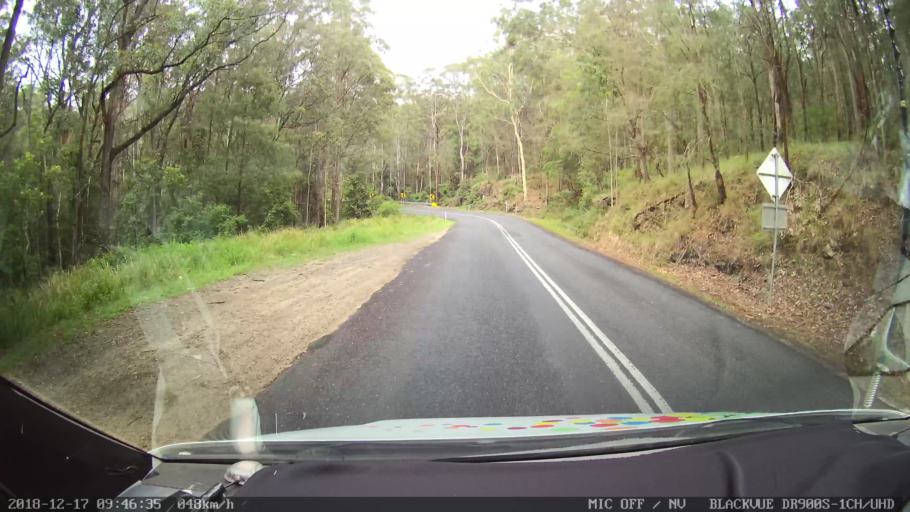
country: AU
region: New South Wales
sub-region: Tenterfield Municipality
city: Carrolls Creek
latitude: -28.9272
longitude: 152.3339
